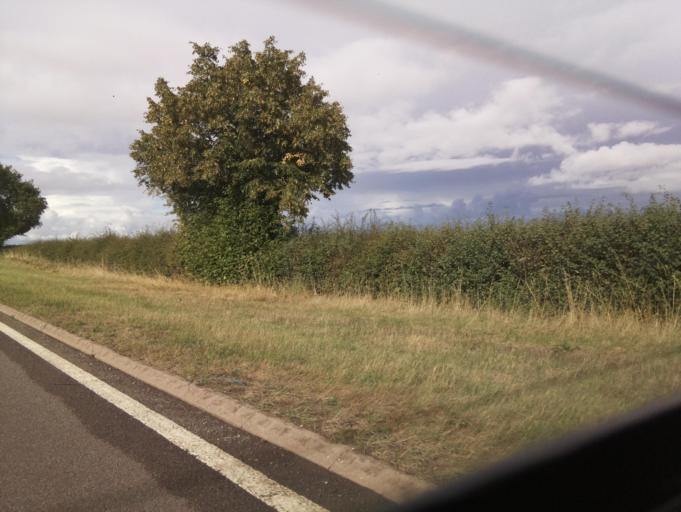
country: GB
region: England
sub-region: Shropshire
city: Bridgnorth
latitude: 52.5867
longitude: -2.3974
